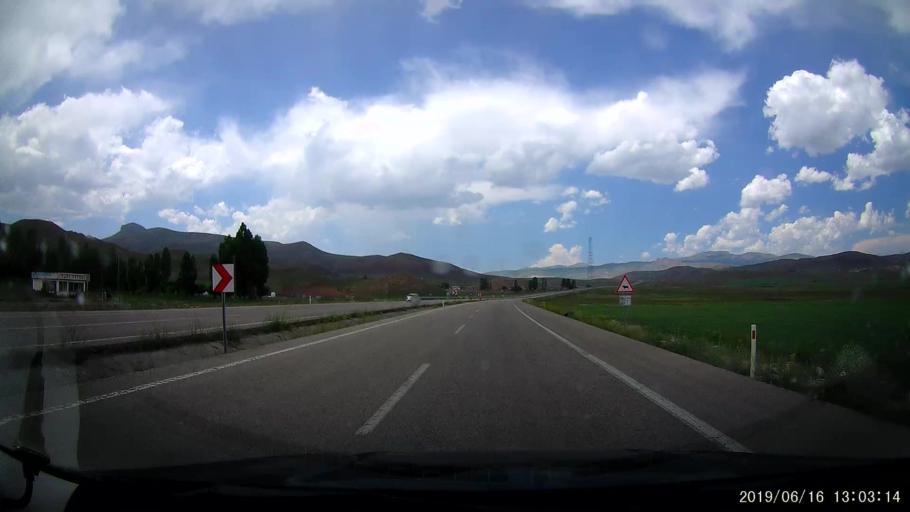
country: TR
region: Agri
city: Sulucem
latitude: 39.5796
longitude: 43.7945
